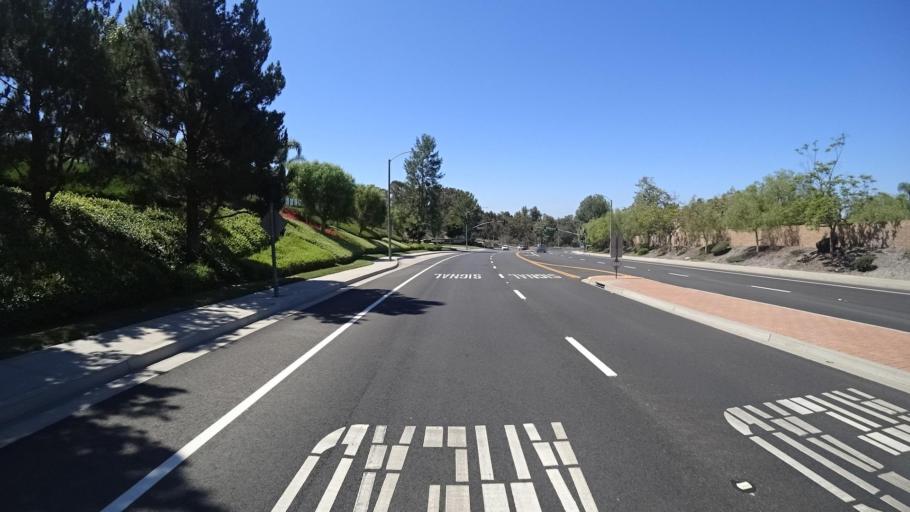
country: US
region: California
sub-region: Orange County
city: Villa Park
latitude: 33.8258
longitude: -117.7924
